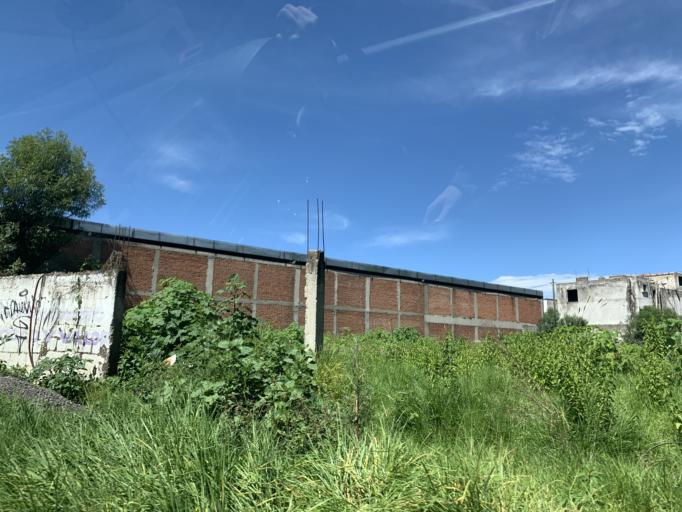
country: MX
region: Puebla
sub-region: Cuautlancingo
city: Barrio de Nuevo Leon
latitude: 19.0825
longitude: -98.2818
